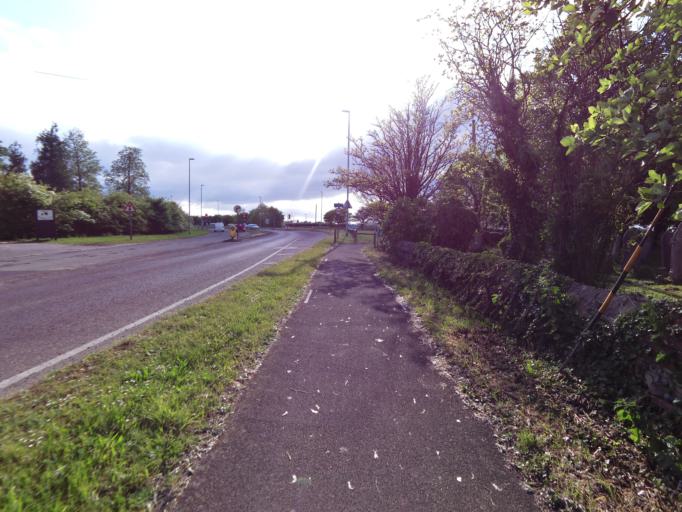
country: GB
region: England
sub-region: Cambridgeshire
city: Fulbourn
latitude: 52.2162
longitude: 0.2178
